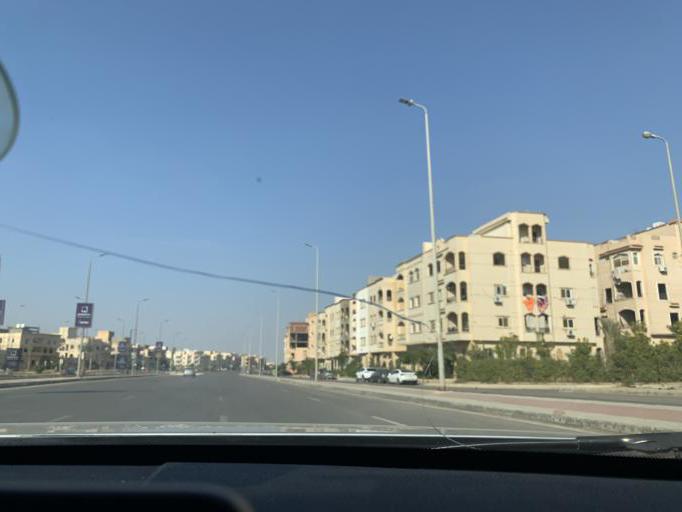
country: EG
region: Muhafazat al Qahirah
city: Cairo
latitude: 30.0016
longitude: 31.4689
